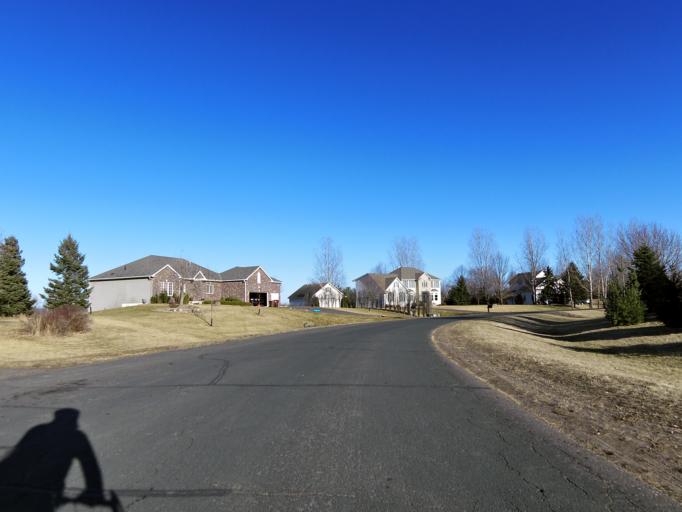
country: US
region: Wisconsin
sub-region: Saint Croix County
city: North Hudson
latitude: 44.9843
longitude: -92.7885
